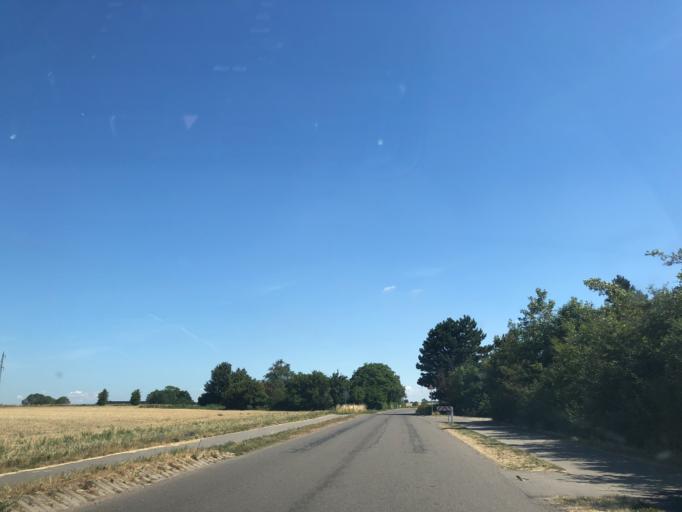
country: DK
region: Zealand
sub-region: Slagelse Kommune
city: Forlev
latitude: 55.3758
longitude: 11.2440
